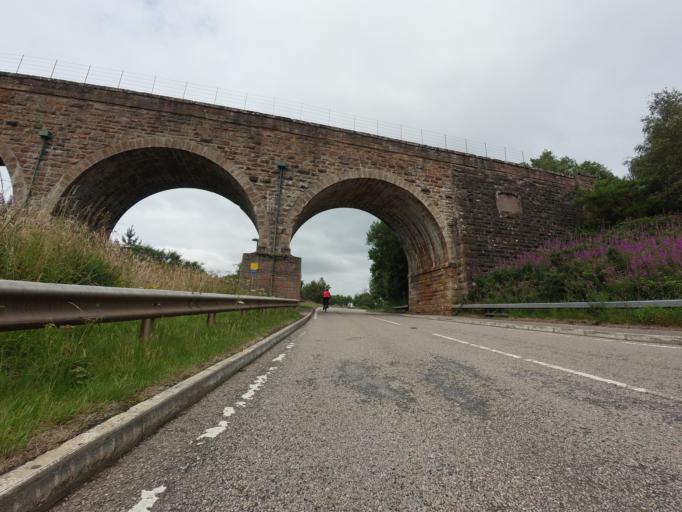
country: GB
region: Scotland
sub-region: Highland
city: Evanton
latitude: 57.9242
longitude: -4.4002
